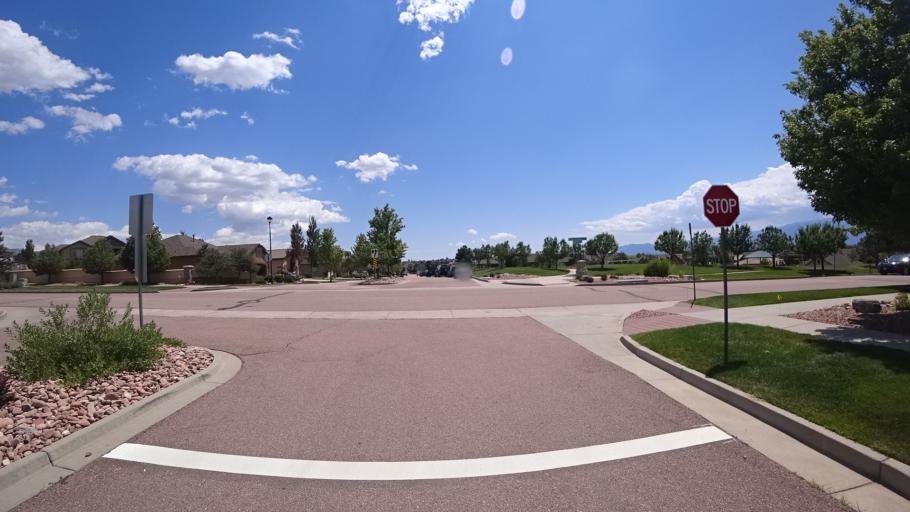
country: US
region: Colorado
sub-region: El Paso County
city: Black Forest
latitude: 38.9702
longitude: -104.7598
